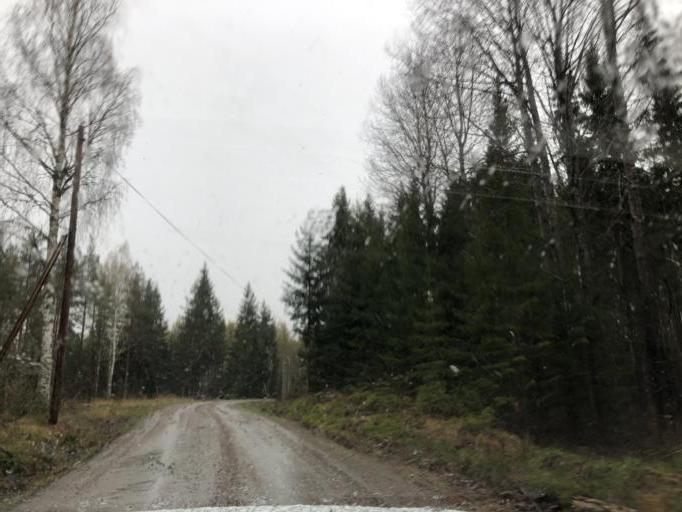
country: SE
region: Uppsala
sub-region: Heby Kommun
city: Tarnsjo
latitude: 60.2039
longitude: 16.8904
